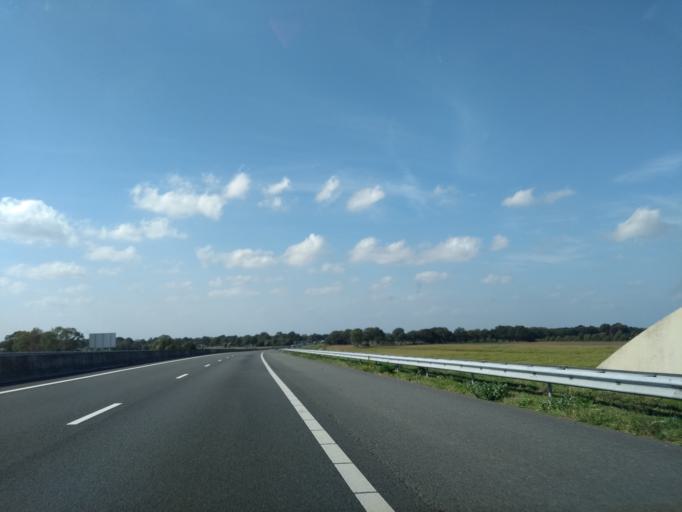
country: NL
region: Overijssel
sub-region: Gemeente Wierden
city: Wierden
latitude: 52.3265
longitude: 6.6261
